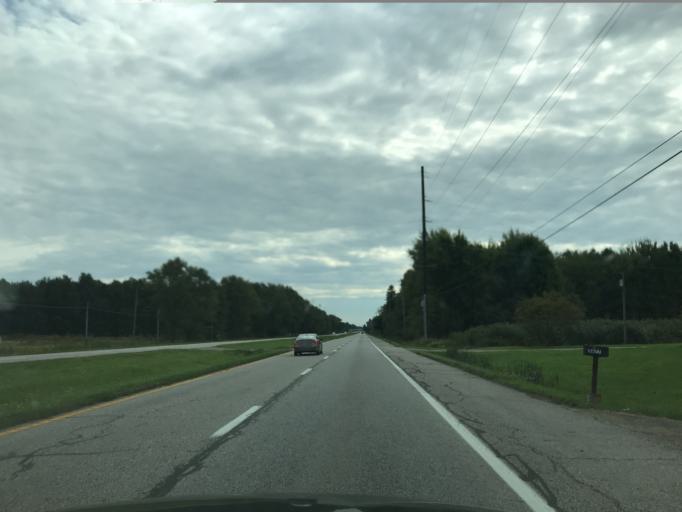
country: US
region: Ohio
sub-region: Trumbull County
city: Leavittsburg
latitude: 41.2715
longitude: -80.8942
